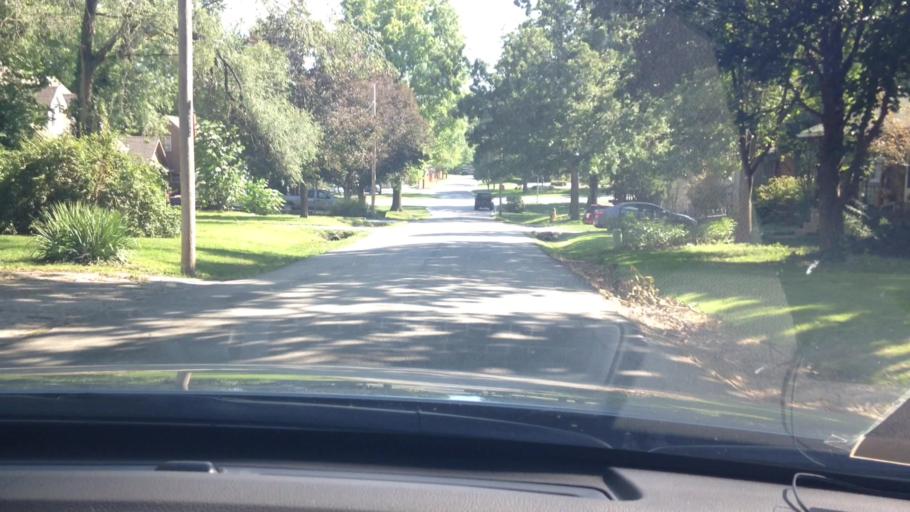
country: US
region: Kansas
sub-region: Johnson County
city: Shawnee
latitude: 39.0234
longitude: -94.7291
